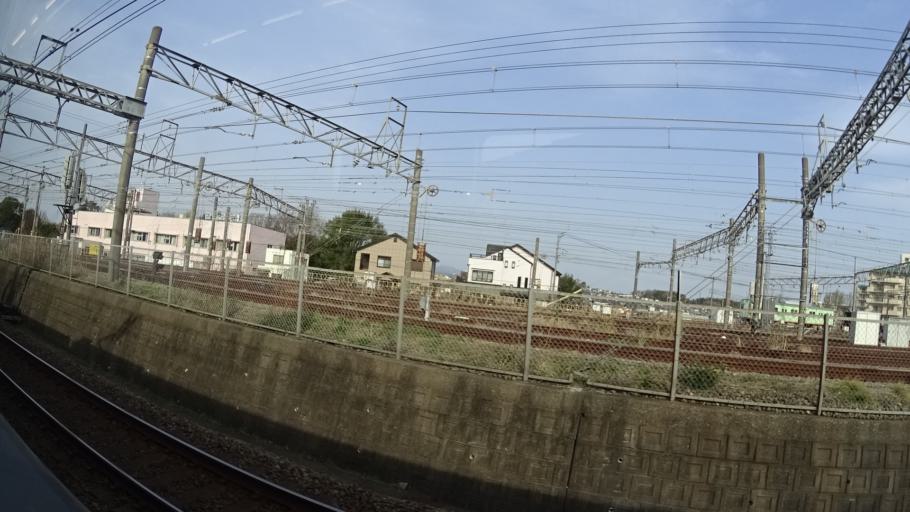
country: JP
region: Kanagawa
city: Zama
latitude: 35.4654
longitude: 139.4124
